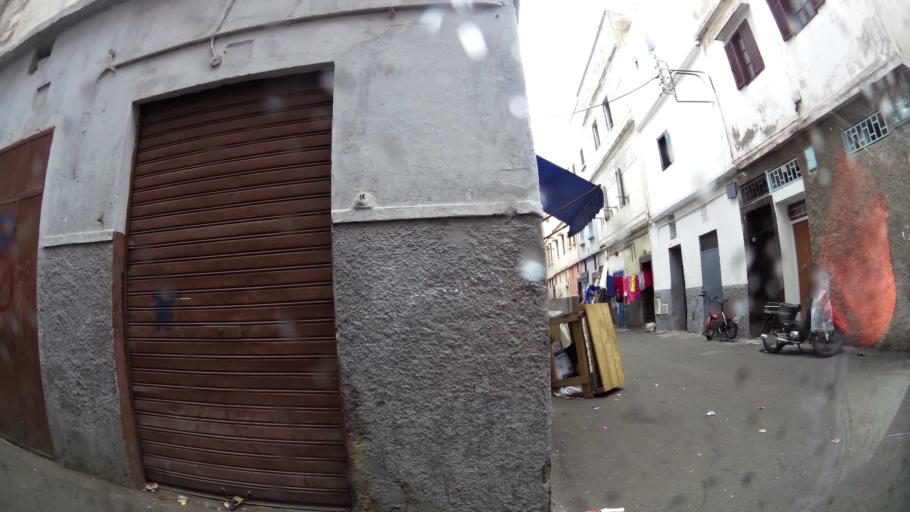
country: MA
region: Grand Casablanca
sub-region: Casablanca
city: Casablanca
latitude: 33.5680
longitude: -7.6055
